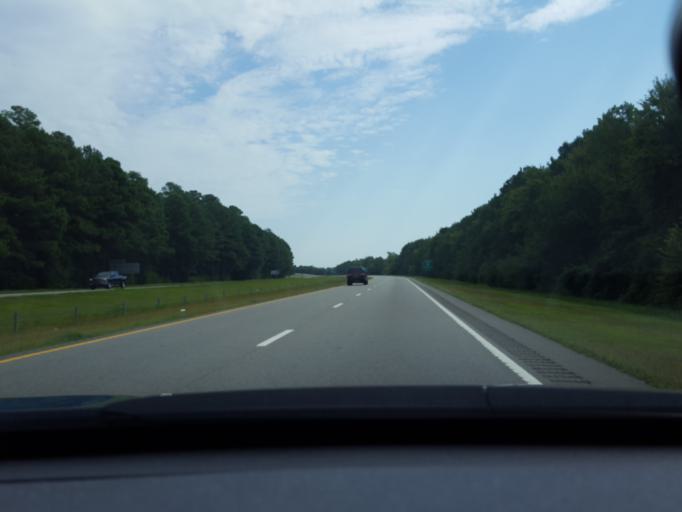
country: US
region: North Carolina
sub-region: Chowan County
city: Edenton
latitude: 36.0706
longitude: -76.6251
